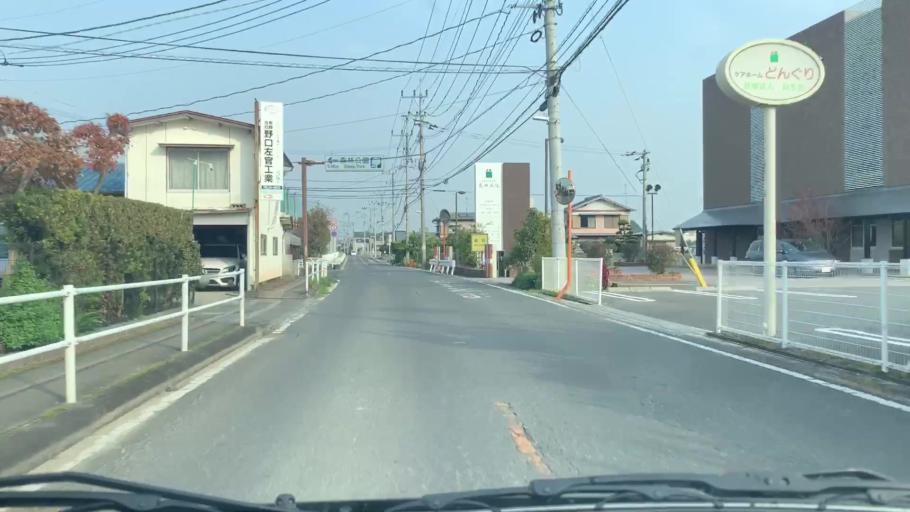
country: JP
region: Saga Prefecture
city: Saga-shi
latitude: 33.2389
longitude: 130.2585
